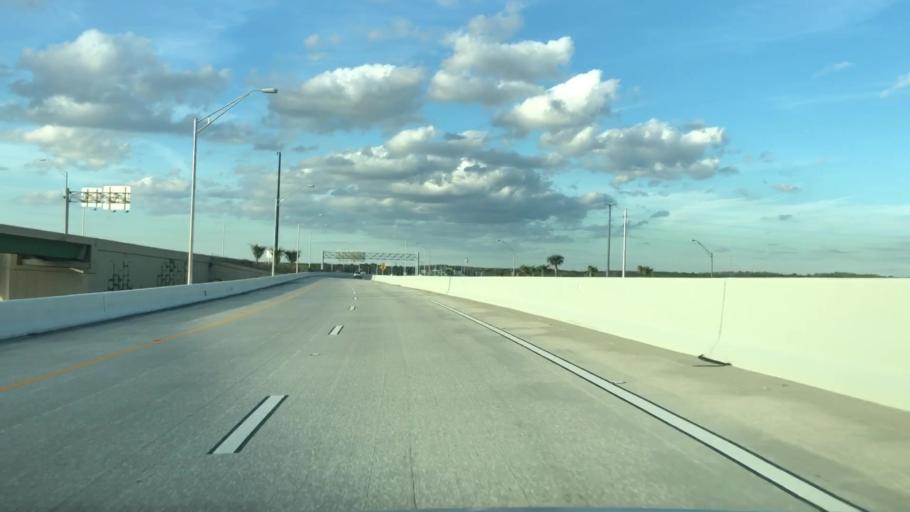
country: US
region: Florida
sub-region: Osceola County
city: Buenaventura Lakes
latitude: 28.3719
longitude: -81.3085
